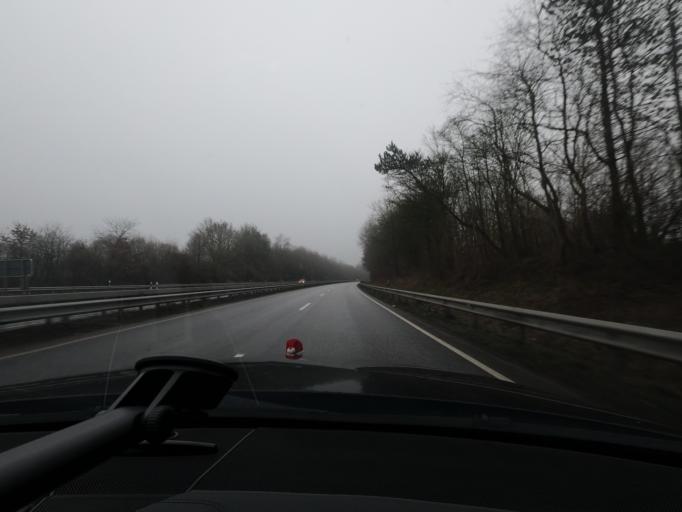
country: DE
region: Schleswig-Holstein
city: Jarplund-Weding
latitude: 54.7558
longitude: 9.4296
